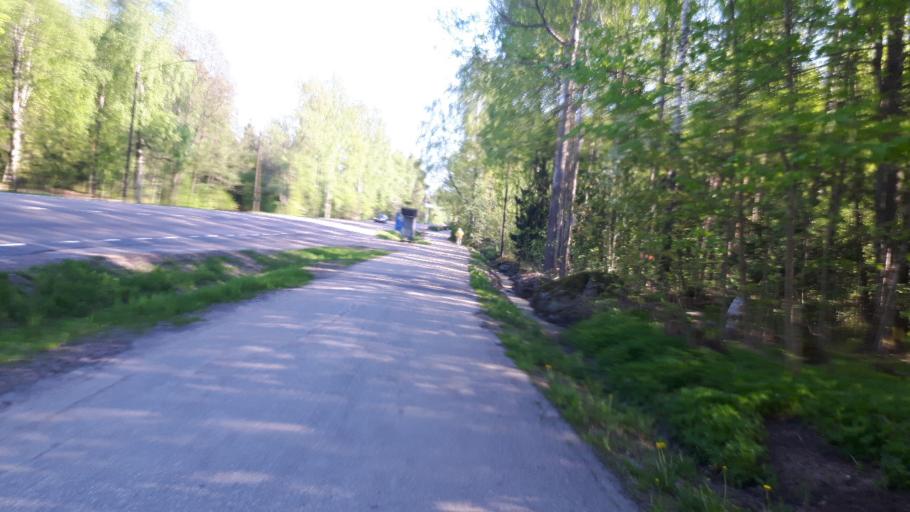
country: FI
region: Kymenlaakso
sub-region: Kotka-Hamina
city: Kotka
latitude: 60.4526
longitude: 26.8941
